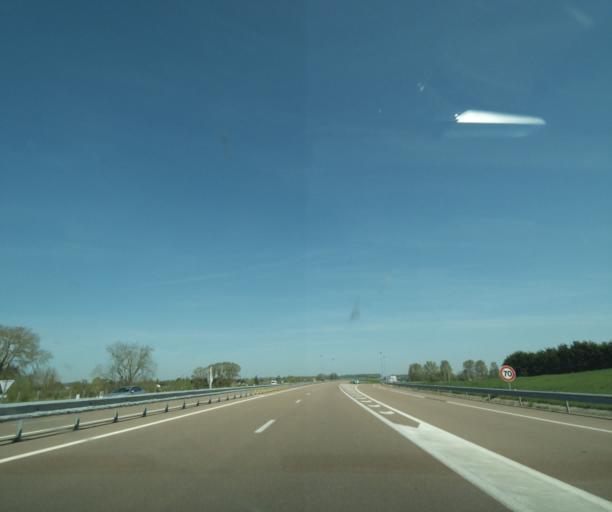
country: FR
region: Bourgogne
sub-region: Departement de la Nievre
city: Magny-Cours
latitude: 46.8702
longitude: 3.1519
